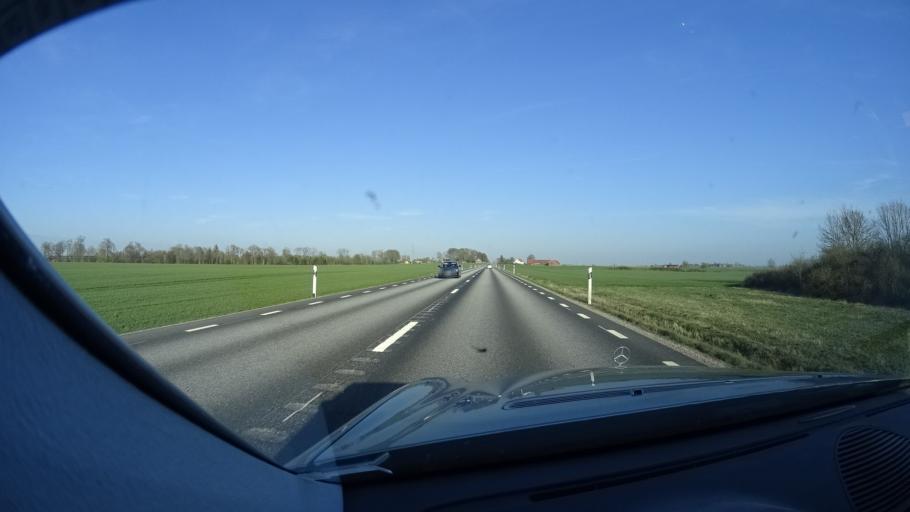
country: SE
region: Skane
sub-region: Eslovs Kommun
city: Eslov
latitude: 55.8612
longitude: 13.2441
